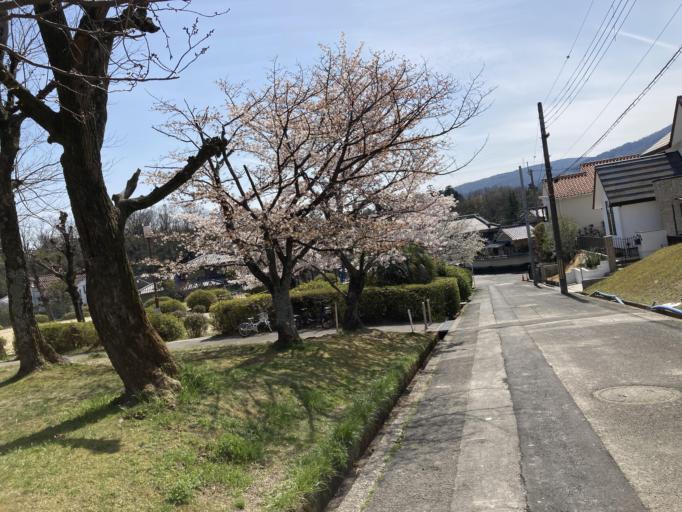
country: JP
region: Nara
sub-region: Ikoma-shi
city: Ikoma
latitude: 34.6823
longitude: 135.7136
